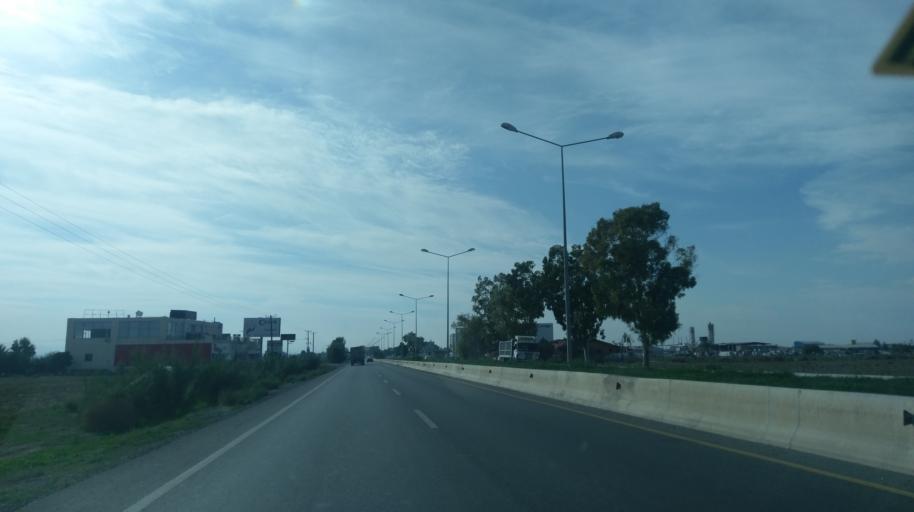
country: CY
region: Lefkosia
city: Nicosia
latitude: 35.2168
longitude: 33.4552
